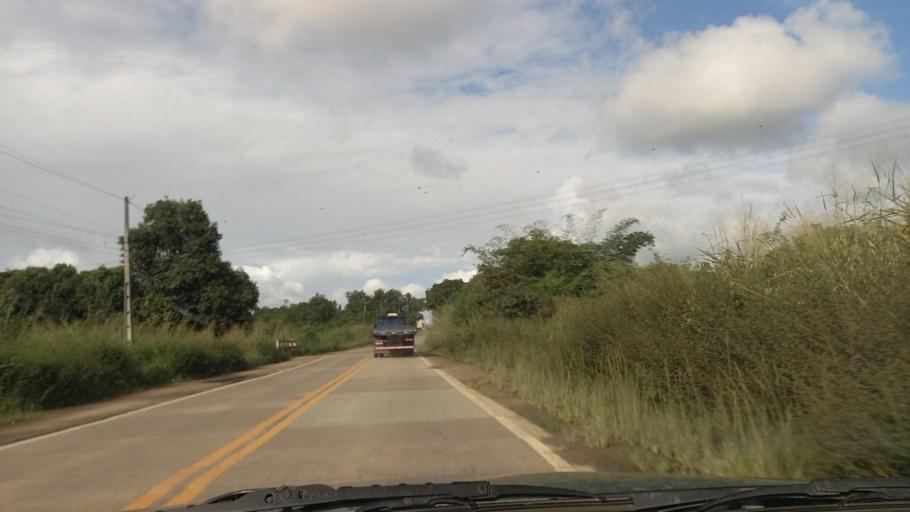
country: BR
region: Pernambuco
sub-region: Palmares
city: Palmares
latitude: -8.6910
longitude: -35.6129
